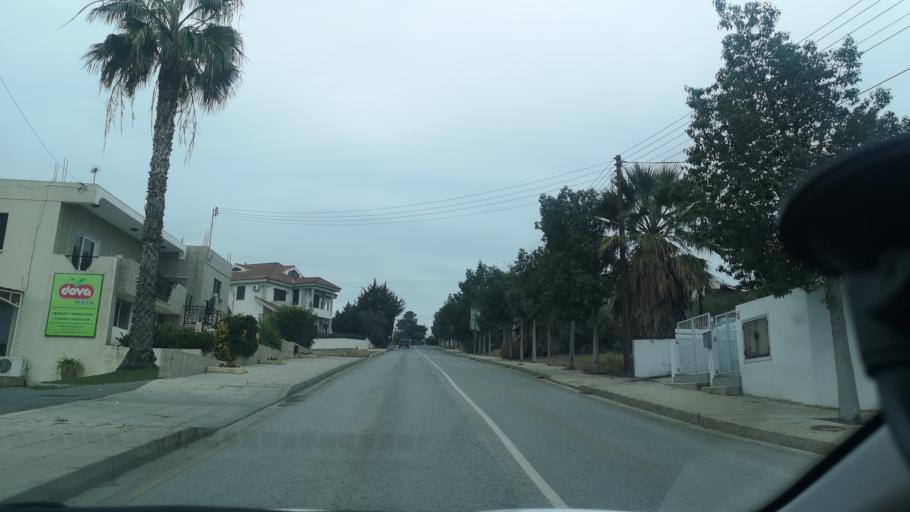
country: CY
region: Lefkosia
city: Tseri
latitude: 35.0755
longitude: 33.3200
